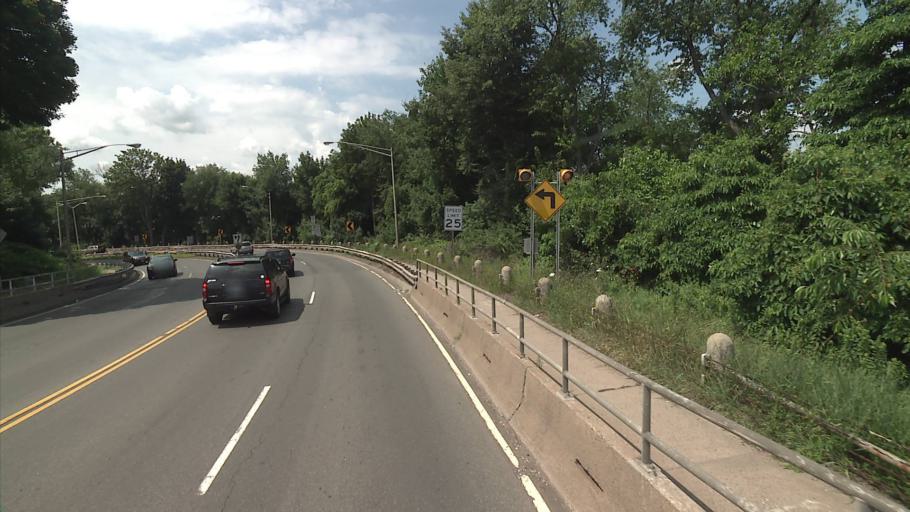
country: US
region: Connecticut
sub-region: Middlesex County
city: Middletown
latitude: 41.5677
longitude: -72.6540
